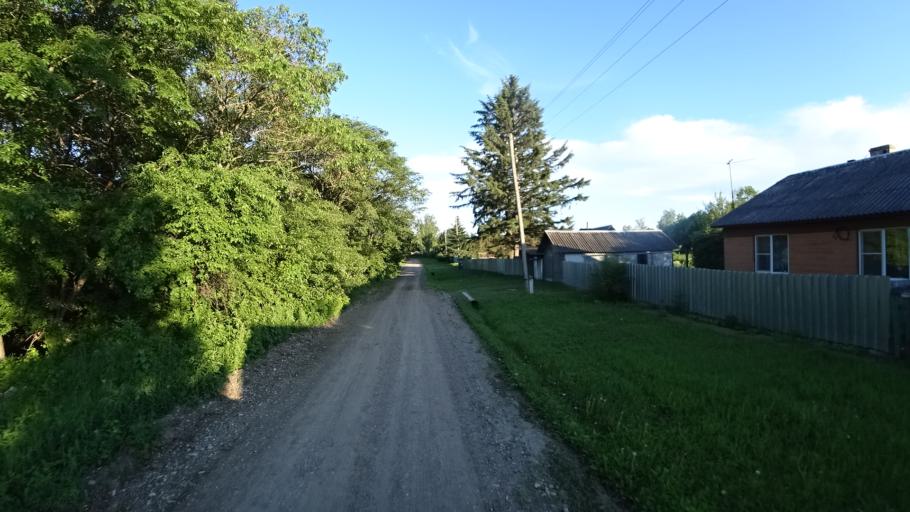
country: RU
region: Khabarovsk Krai
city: Khor
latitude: 47.8558
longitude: 135.0022
